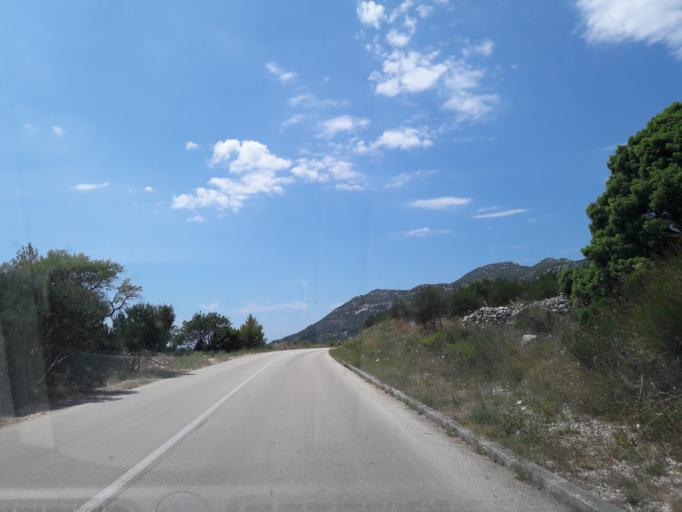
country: HR
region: Dubrovacko-Neretvanska
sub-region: Grad Korcula
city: Zrnovo
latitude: 42.9815
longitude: 17.1084
